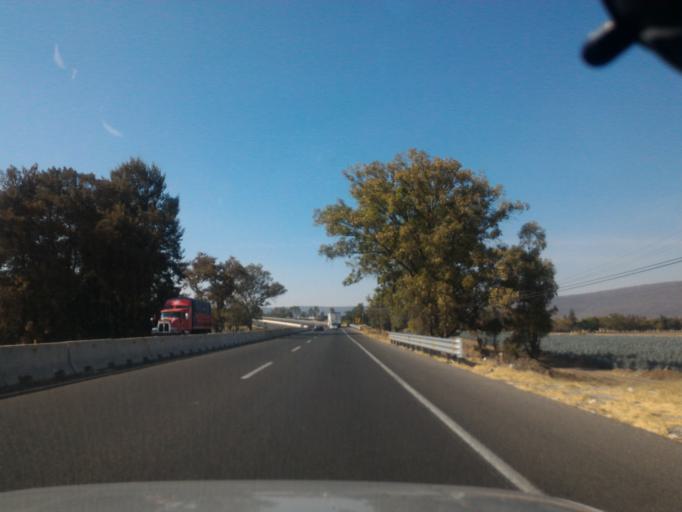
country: MX
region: Jalisco
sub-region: Poncitlan
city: Cuitzeo (La Estancia)
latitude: 20.3627
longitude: -102.8057
